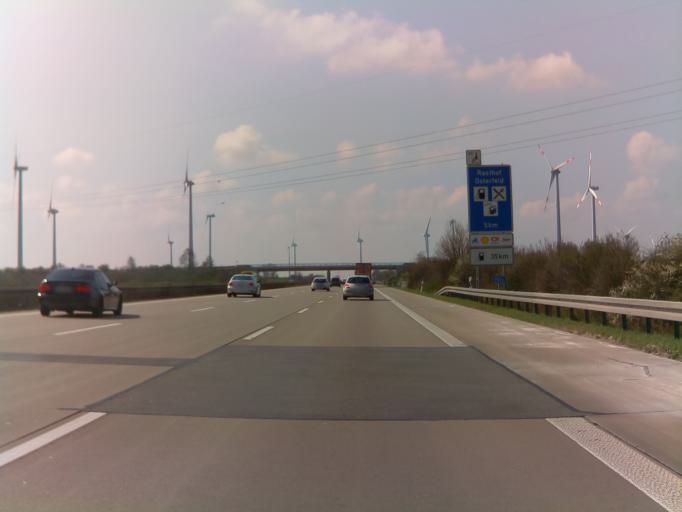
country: DE
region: Saxony-Anhalt
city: Nessa
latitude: 51.1469
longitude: 11.9769
